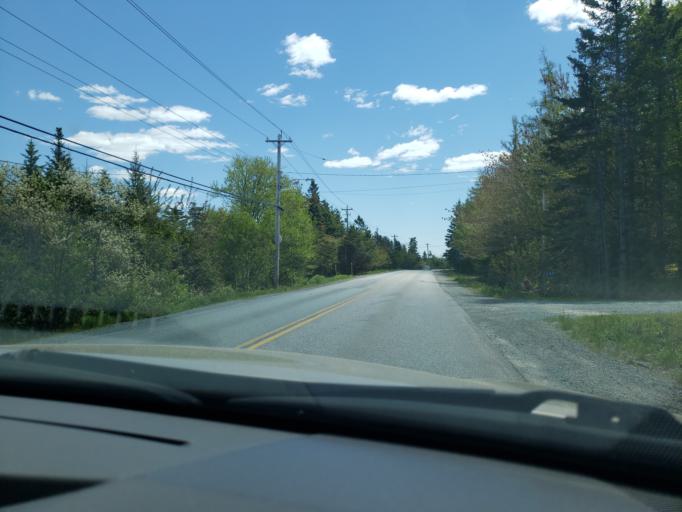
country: CA
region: Nova Scotia
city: Cole Harbour
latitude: 44.7316
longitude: -63.3078
